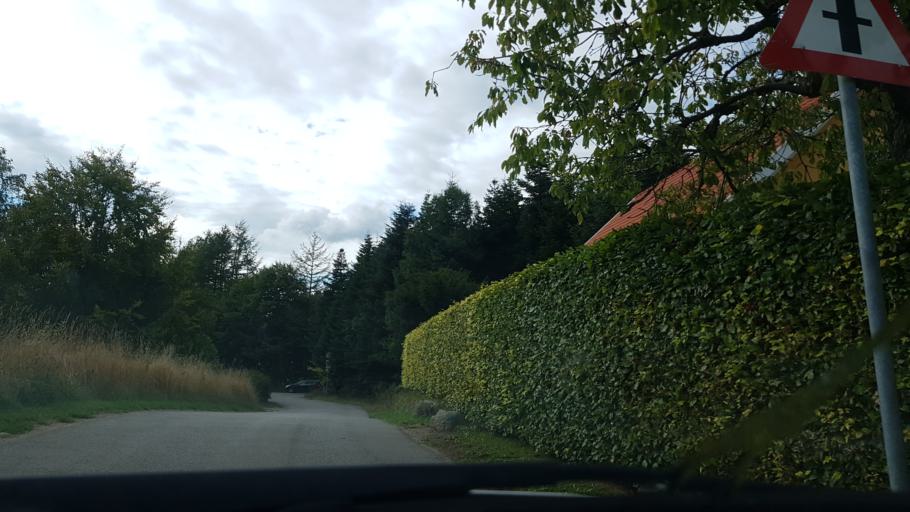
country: DK
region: Capital Region
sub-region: Fredensborg Kommune
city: Niva
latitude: 55.9821
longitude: 12.4805
